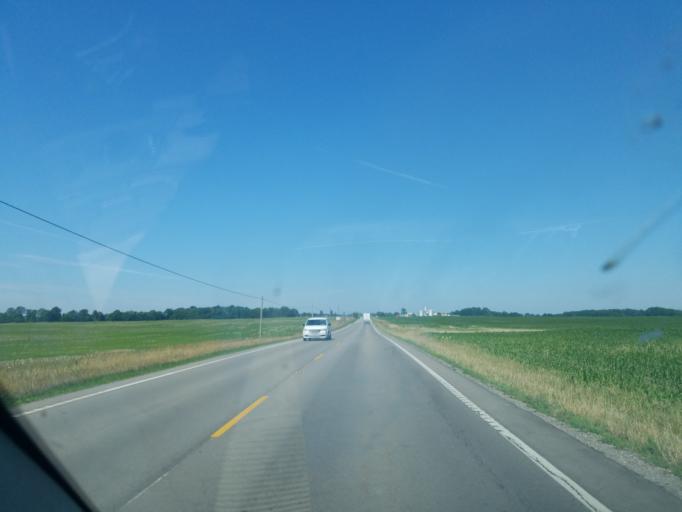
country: US
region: Ohio
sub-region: Shelby County
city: Jackson Center
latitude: 40.4393
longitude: -83.9992
